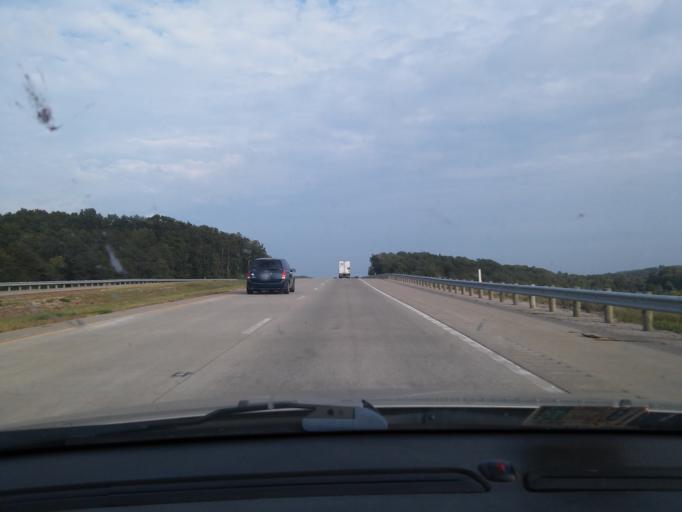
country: US
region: West Virginia
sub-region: Mason County
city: Point Pleasant
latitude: 38.7759
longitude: -82.0592
